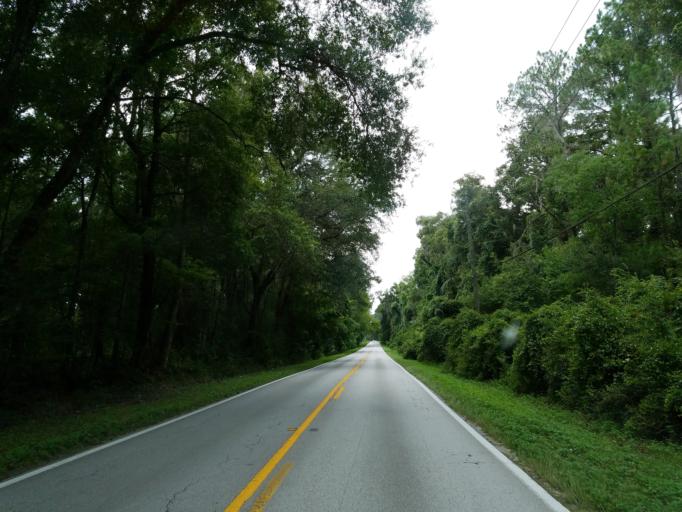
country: US
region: Florida
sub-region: Alachua County
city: Gainesville
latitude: 29.5938
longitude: -82.3512
